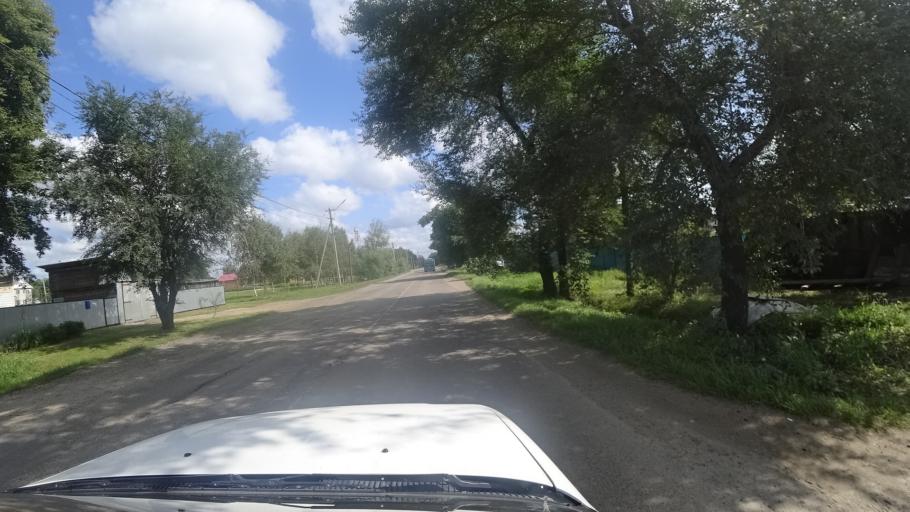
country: RU
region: Primorskiy
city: Dal'nerechensk
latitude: 45.9299
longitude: 133.7618
